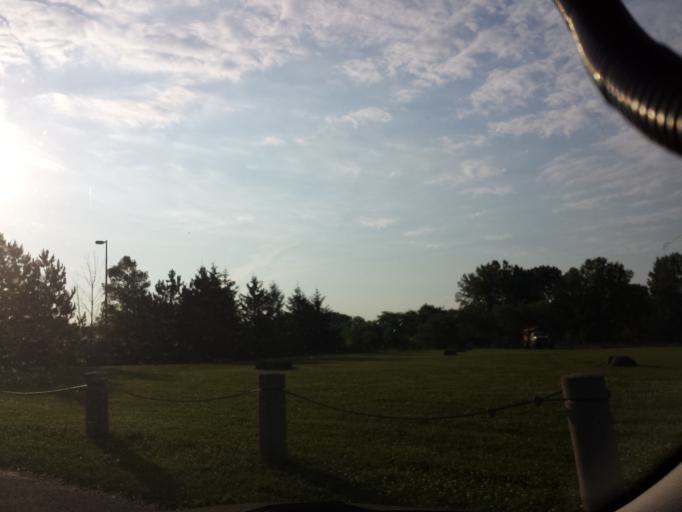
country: CA
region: Ontario
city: Bells Corners
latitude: 45.3506
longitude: -75.8260
